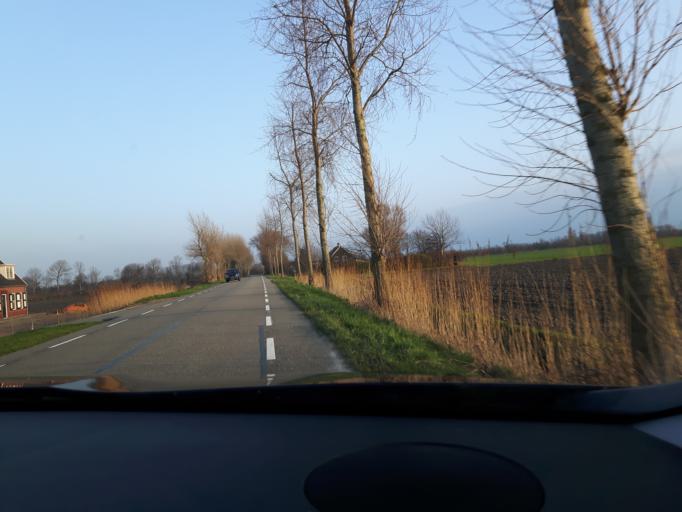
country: NL
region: Zeeland
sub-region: Gemeente Veere
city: Veere
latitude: 51.5799
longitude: 3.5946
